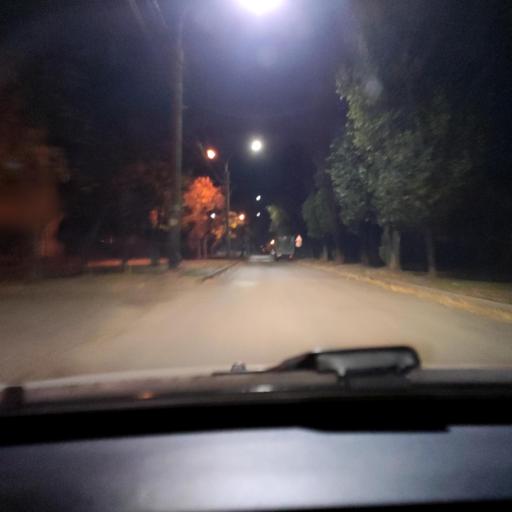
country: RU
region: Voronezj
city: Podgornoye
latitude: 51.7032
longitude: 39.1587
